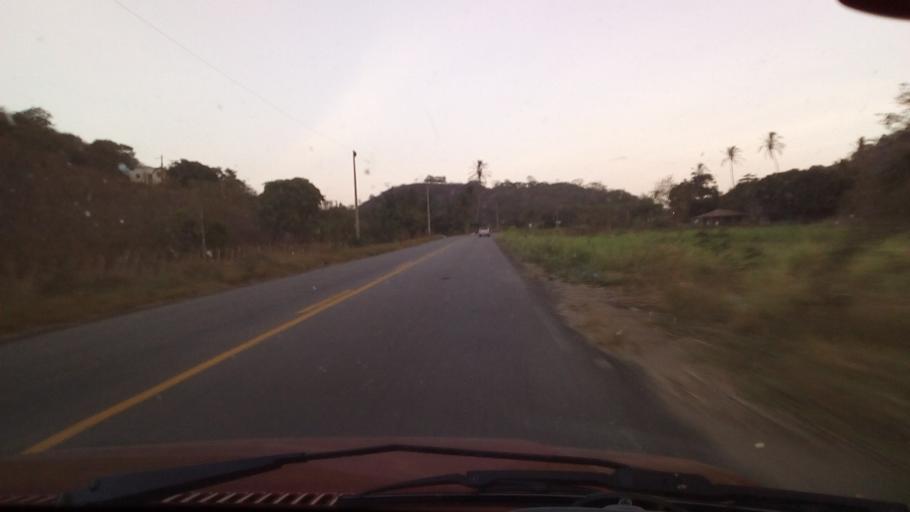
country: BR
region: Paraiba
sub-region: Bananeiras
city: Solanea
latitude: -6.7391
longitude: -35.5349
